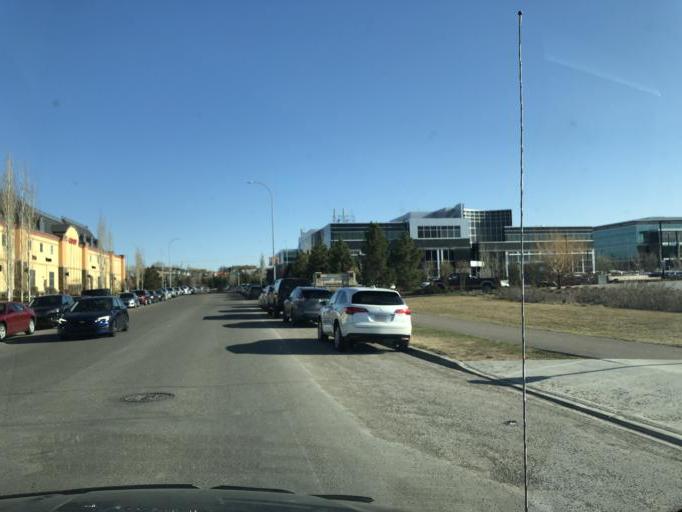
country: CA
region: Alberta
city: Calgary
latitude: 50.9617
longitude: -114.0072
